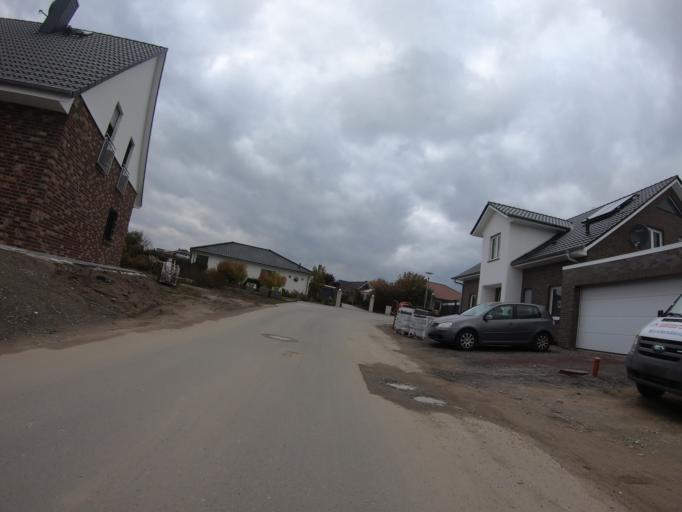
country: DE
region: Lower Saxony
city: Calberlah
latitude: 52.4194
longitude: 10.6287
